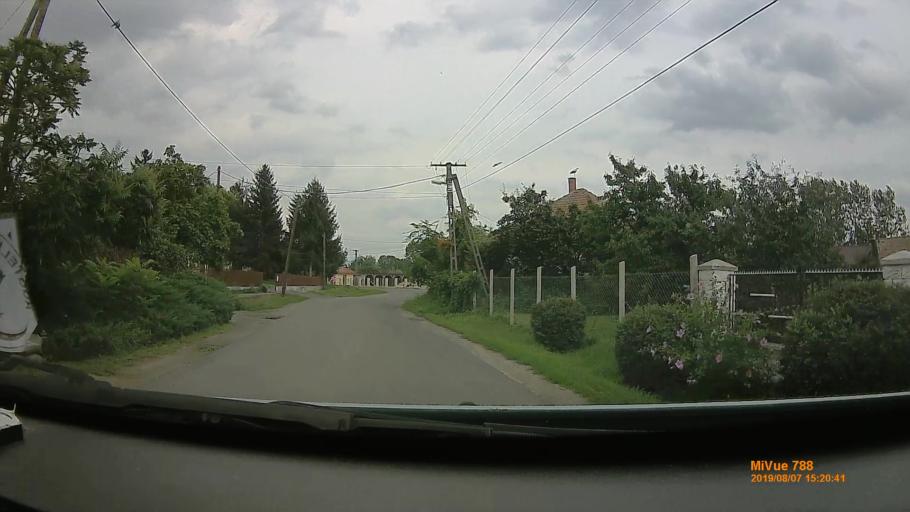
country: HU
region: Borsod-Abauj-Zemplen
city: Encs
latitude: 48.3562
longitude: 21.1500
